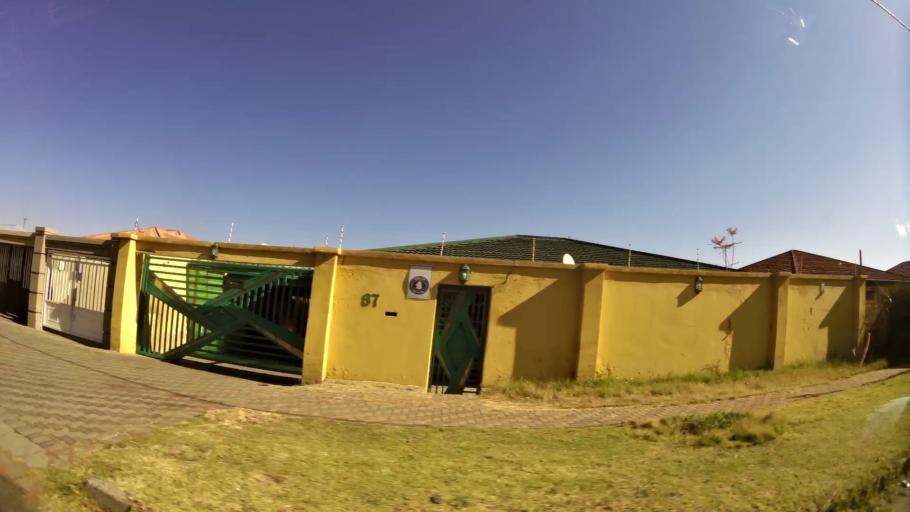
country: ZA
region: Gauteng
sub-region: City of Johannesburg Metropolitan Municipality
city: Johannesburg
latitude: -26.1900
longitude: 27.9832
